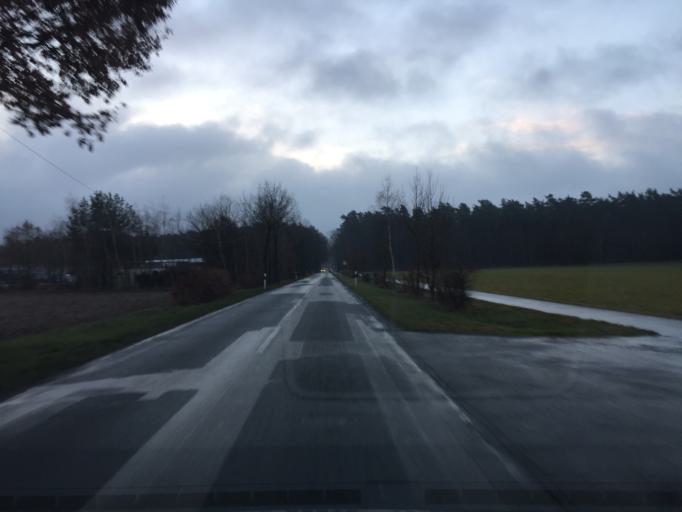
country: DE
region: Lower Saxony
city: Liebenau
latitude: 52.6167
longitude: 9.0734
